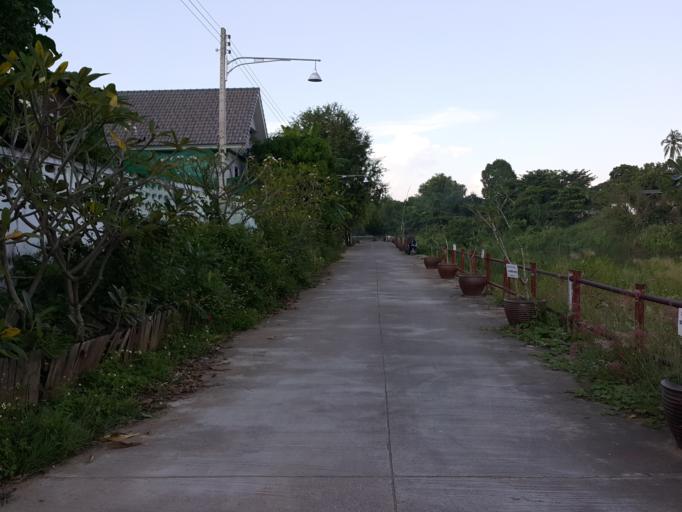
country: TH
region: Lampang
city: Lampang
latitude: 18.2947
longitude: 99.5123
